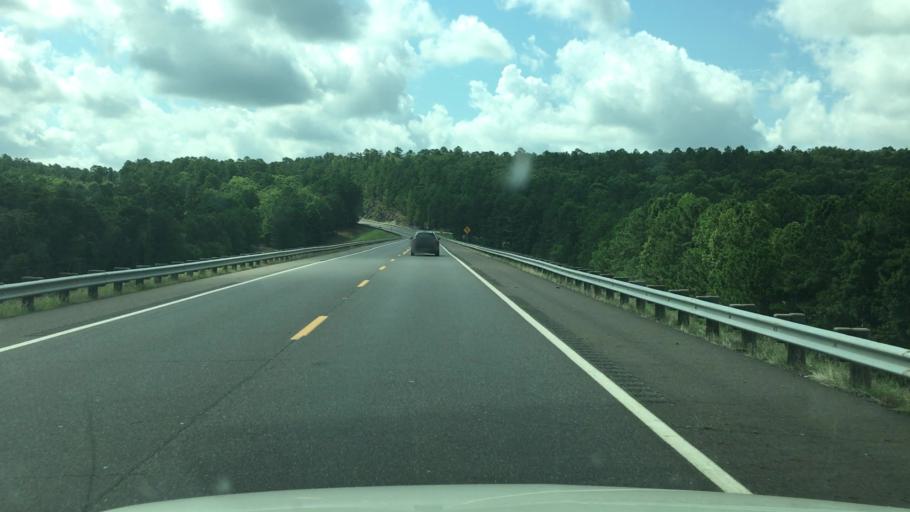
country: US
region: Arkansas
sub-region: Clark County
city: Arkadelphia
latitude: 34.2359
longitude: -93.1017
